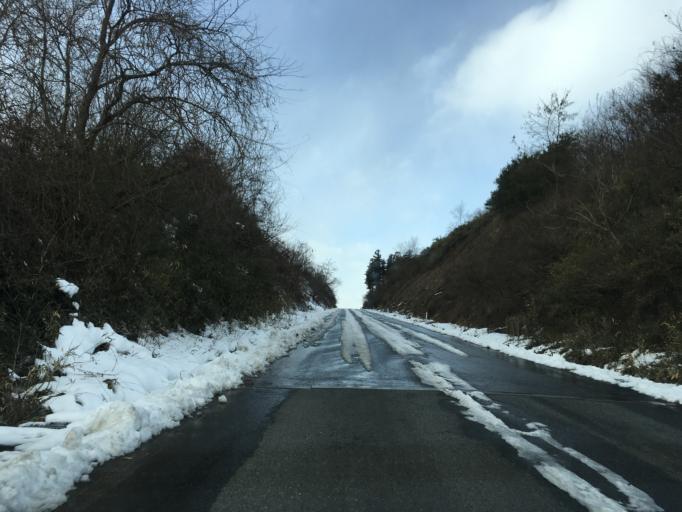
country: JP
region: Iwate
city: Ichinoseki
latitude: 38.8620
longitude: 141.1975
